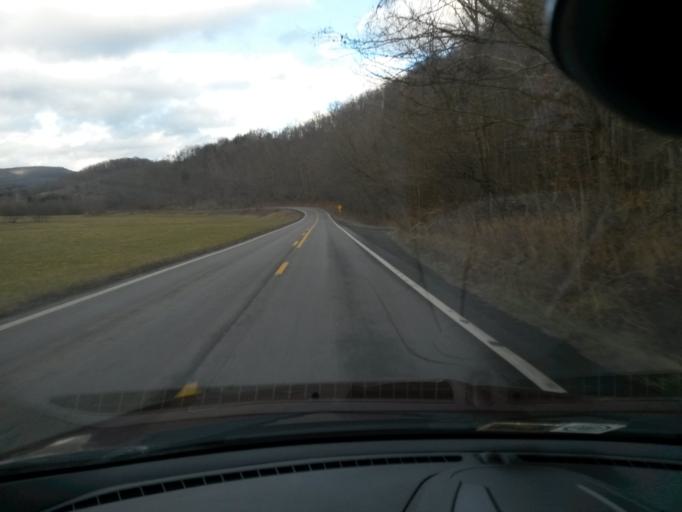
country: US
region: West Virginia
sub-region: Monroe County
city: Union
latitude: 37.5500
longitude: -80.5734
